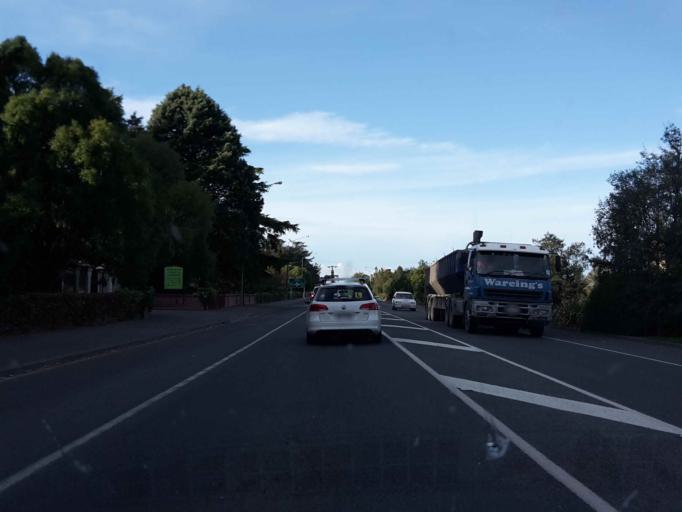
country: NZ
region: Canterbury
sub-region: Ashburton District
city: Ashburton
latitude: -43.8999
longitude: 171.7533
